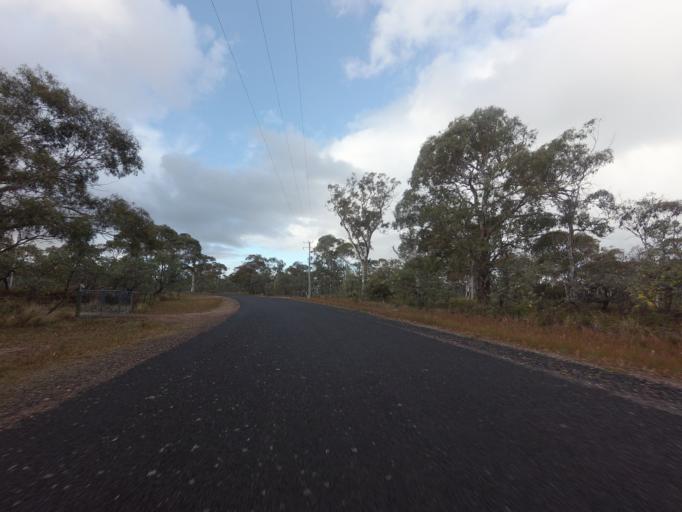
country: AU
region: Tasmania
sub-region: Break O'Day
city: St Helens
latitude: -42.1075
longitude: 148.0743
